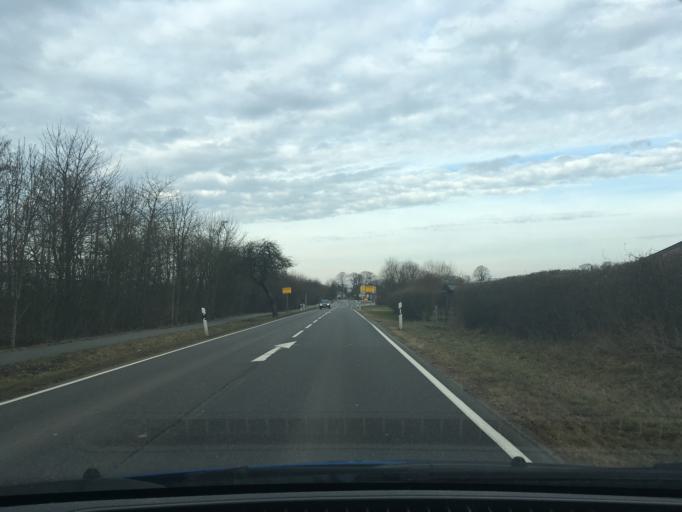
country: DE
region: Mecklenburg-Vorpommern
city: Zarrentin
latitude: 53.5437
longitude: 10.9066
